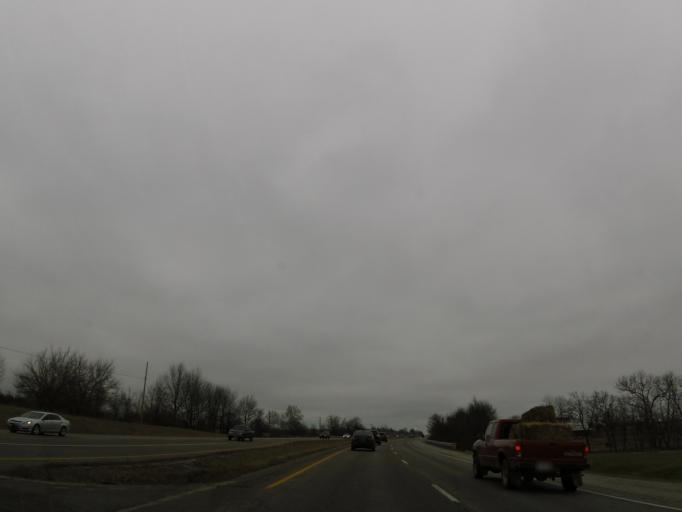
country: US
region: Kentucky
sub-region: Anderson County
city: Lawrenceburg
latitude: 38.0446
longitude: -84.9139
